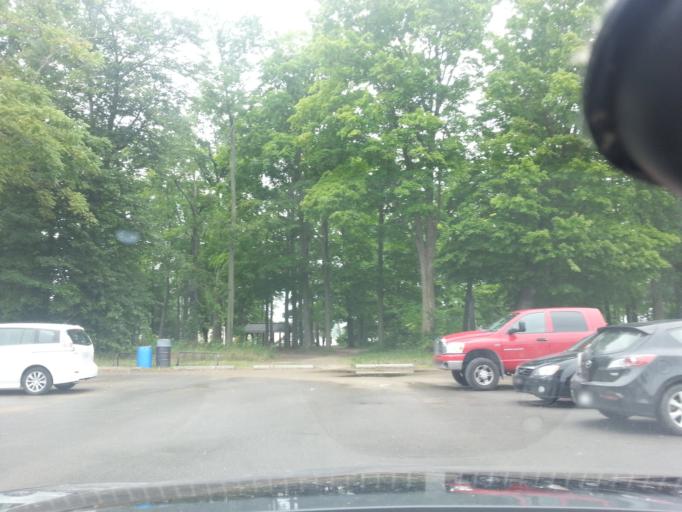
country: CA
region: Ontario
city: Prince Edward
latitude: 43.9099
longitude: -77.2715
